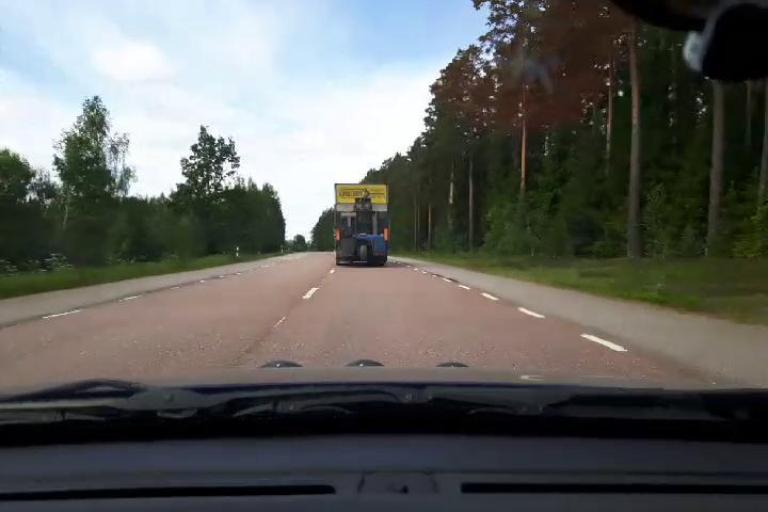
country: SE
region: Uppsala
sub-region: Osthammars Kommun
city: Bjorklinge
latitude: 60.1447
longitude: 17.5011
